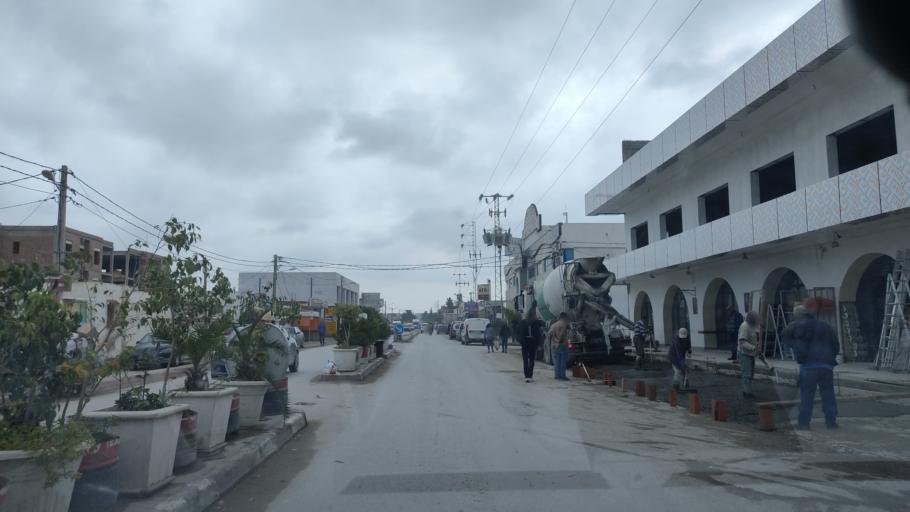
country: TN
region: Ariana
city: Ariana
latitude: 36.8870
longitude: 10.2172
